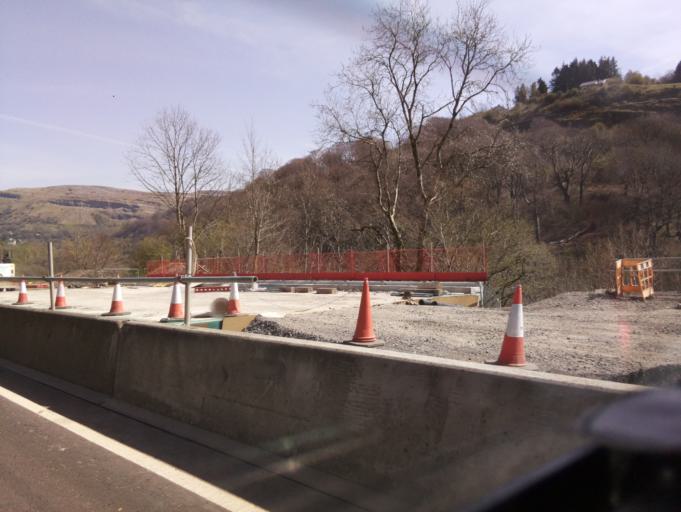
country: GB
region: Wales
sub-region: Monmouthshire
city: Gilwern
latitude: 51.8067
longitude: -3.1358
